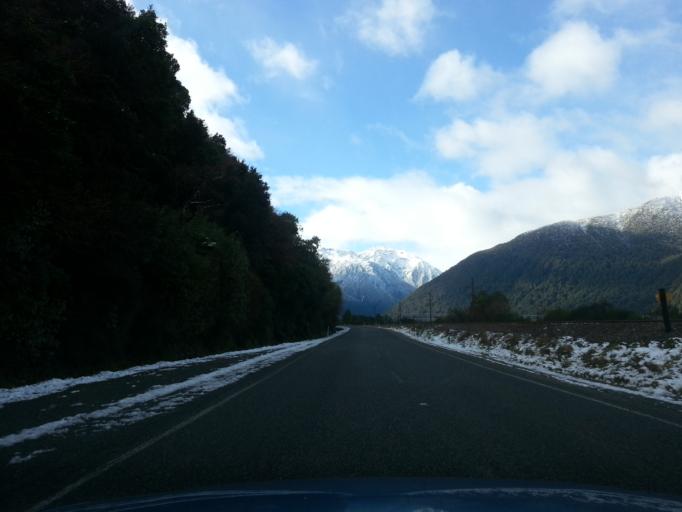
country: NZ
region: West Coast
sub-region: Grey District
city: Greymouth
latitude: -42.7887
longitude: 171.6010
